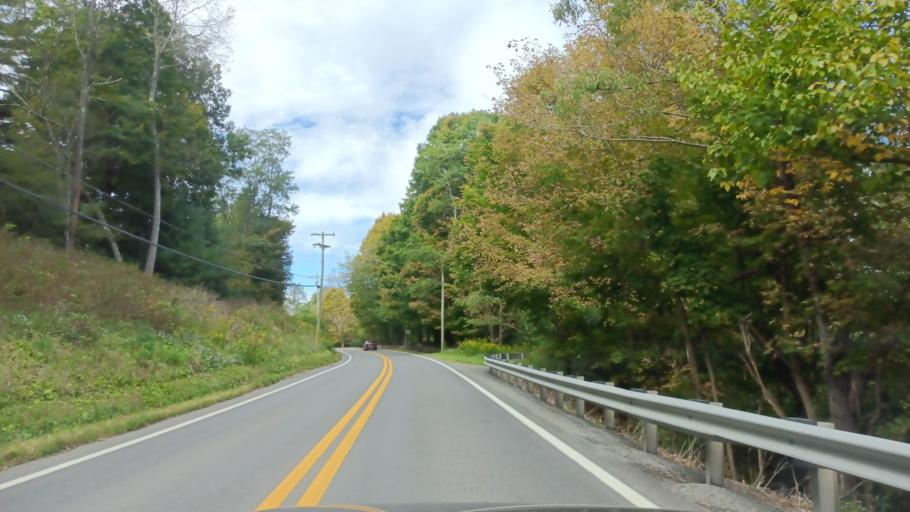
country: US
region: West Virginia
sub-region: Preston County
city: Terra Alta
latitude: 39.3263
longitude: -79.5320
